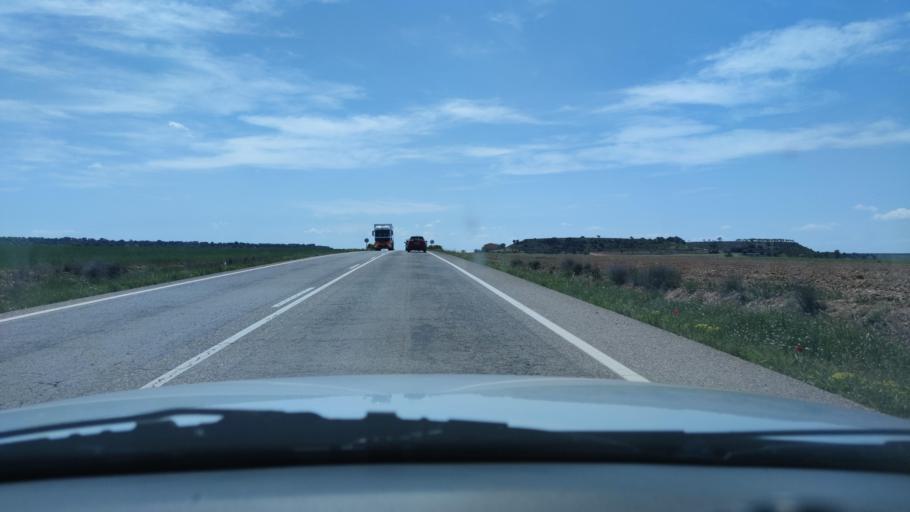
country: ES
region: Catalonia
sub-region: Provincia de Lleida
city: Mont-roig del Camp
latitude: 41.7032
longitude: 1.1803
